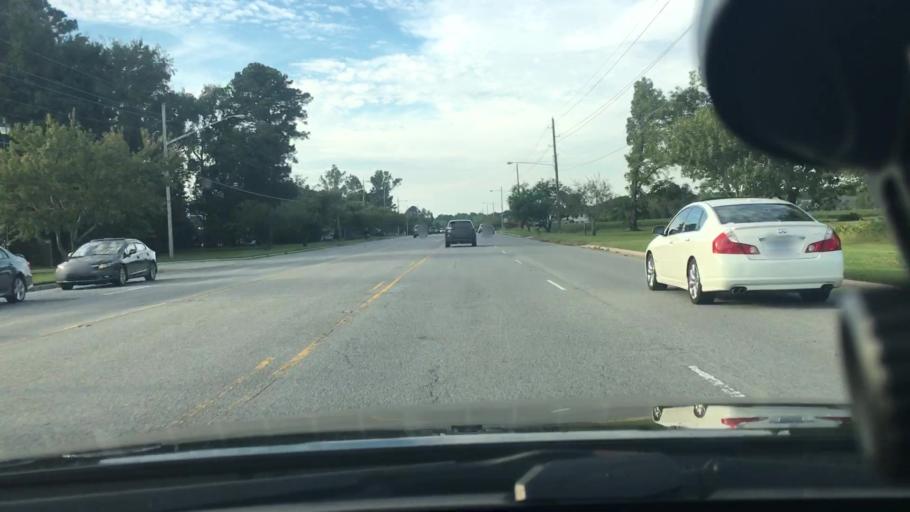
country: US
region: North Carolina
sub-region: Pitt County
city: Windsor
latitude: 35.5716
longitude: -77.3528
